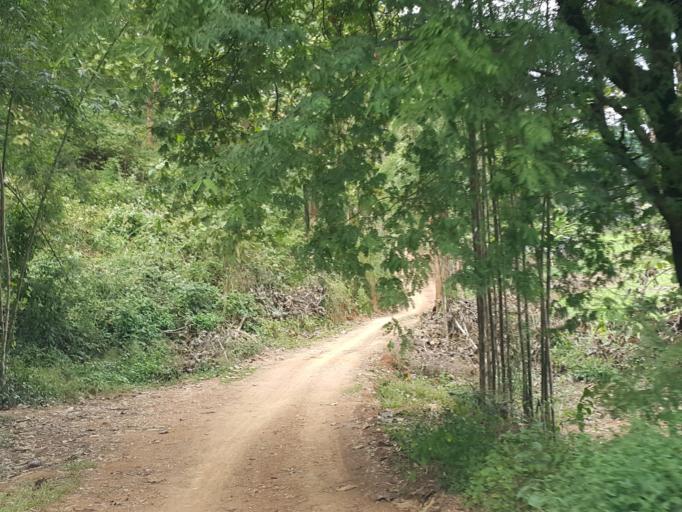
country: TH
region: Lampang
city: Chae Hom
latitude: 18.5673
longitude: 99.4456
